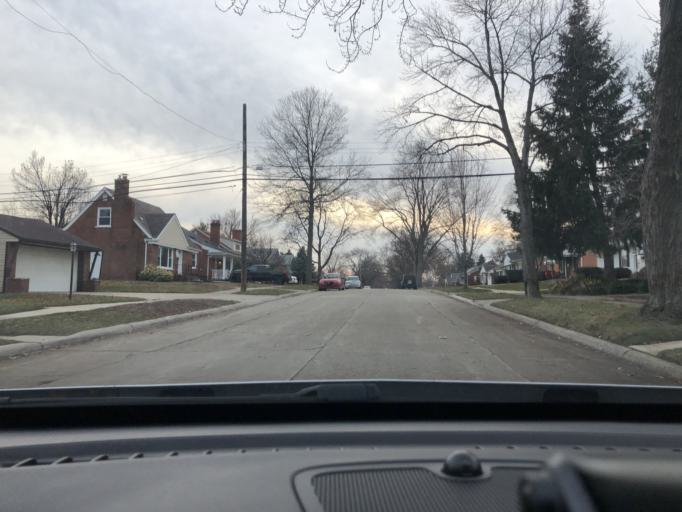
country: US
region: Michigan
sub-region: Wayne County
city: Allen Park
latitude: 42.2912
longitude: -83.2256
